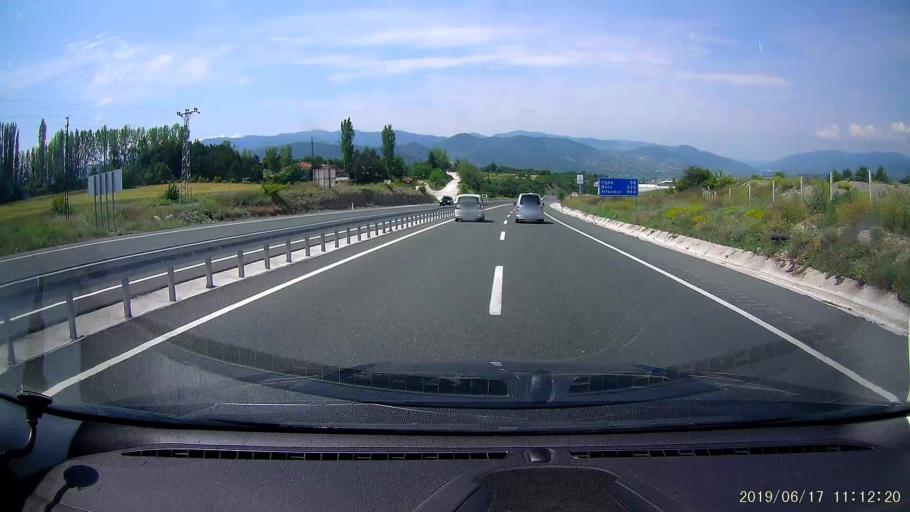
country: TR
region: Kastamonu
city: Tosya
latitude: 40.9733
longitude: 33.9969
